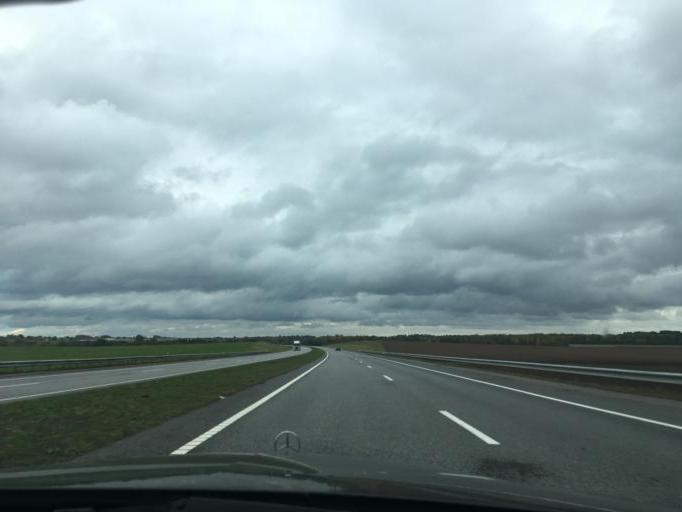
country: BY
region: Vitebsk
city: Kokhanava
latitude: 54.4737
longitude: 29.8736
